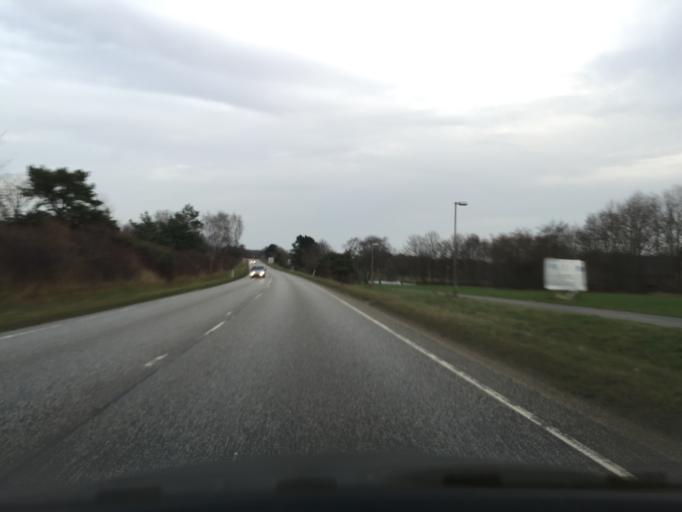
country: DK
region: Central Jutland
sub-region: Viborg Kommune
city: Bjerringbro
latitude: 56.3728
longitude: 9.6306
